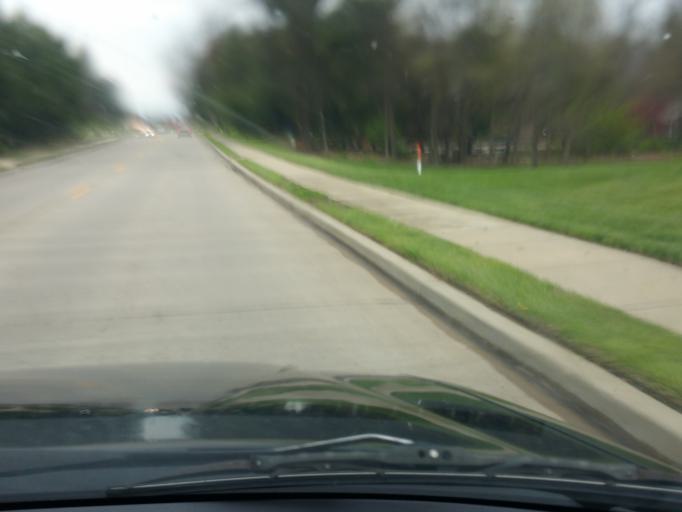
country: US
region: Illinois
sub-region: Madison County
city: Edwardsville
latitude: 38.7813
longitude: -89.9414
